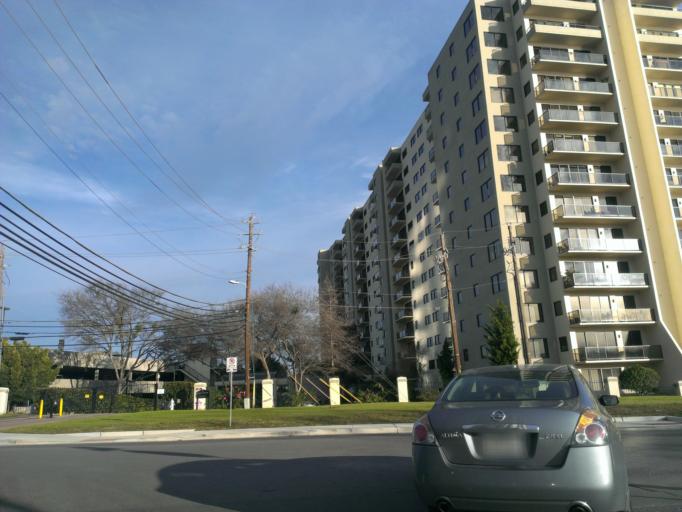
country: US
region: Texas
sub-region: Travis County
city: Austin
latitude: 30.2554
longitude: -97.7389
